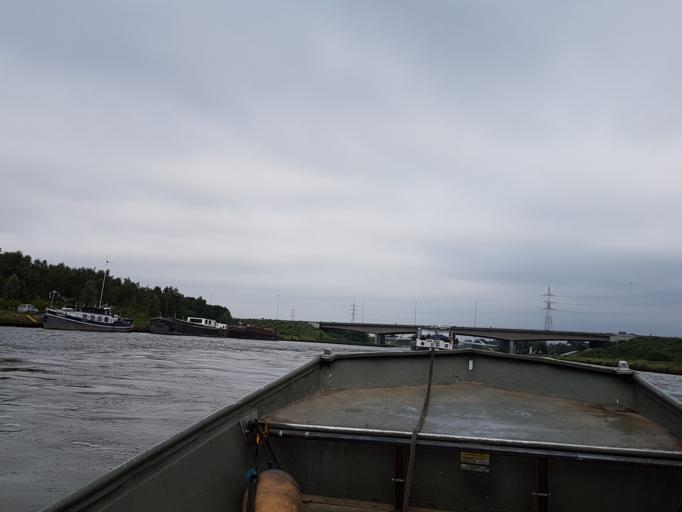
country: BE
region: Flanders
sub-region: Provincie Antwerpen
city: Schilde
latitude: 51.2033
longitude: 4.6110
